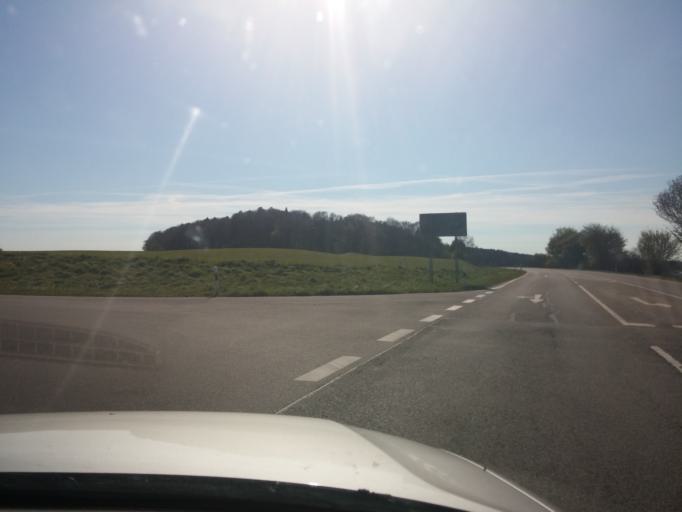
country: DE
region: Baden-Wuerttemberg
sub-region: Tuebingen Region
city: Bad Schussenried
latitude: 48.0244
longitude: 9.6781
